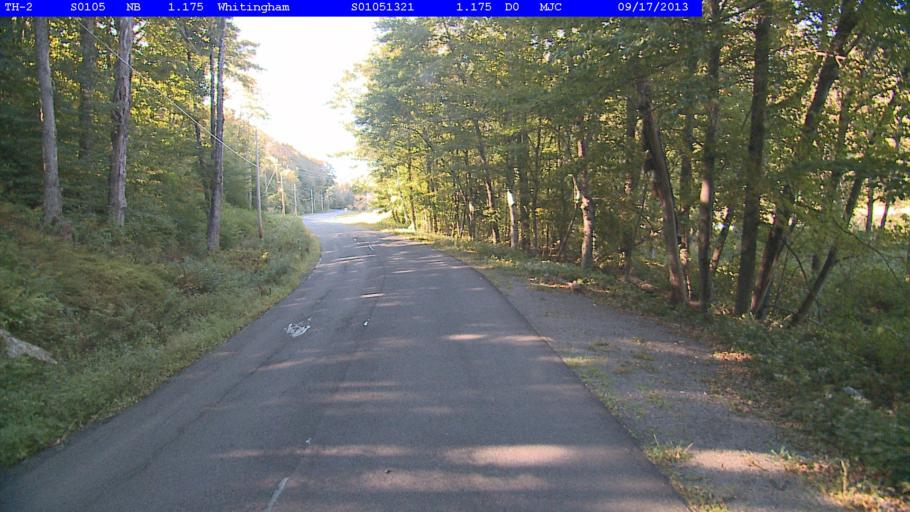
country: US
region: Massachusetts
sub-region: Franklin County
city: Charlemont
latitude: 42.7546
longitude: -72.9284
